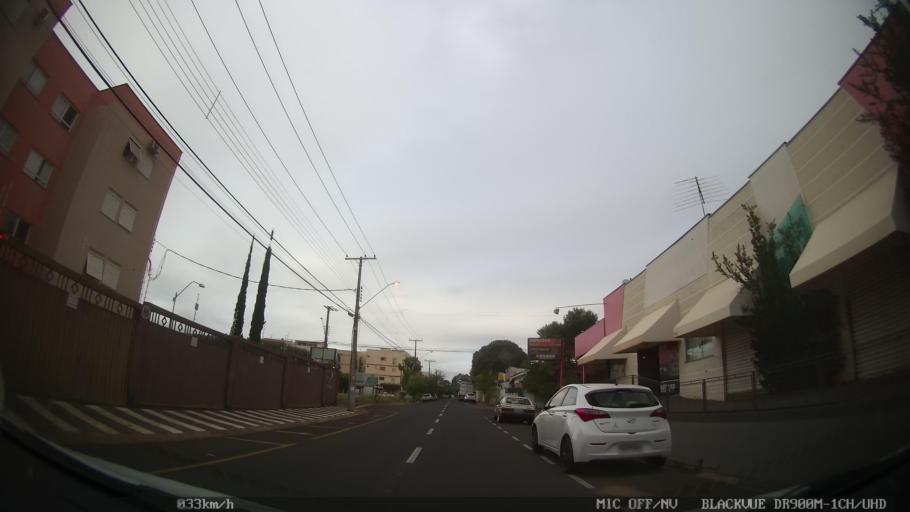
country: BR
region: Sao Paulo
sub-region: Sao Jose Do Rio Preto
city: Sao Jose do Rio Preto
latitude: -20.8382
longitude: -49.3856
